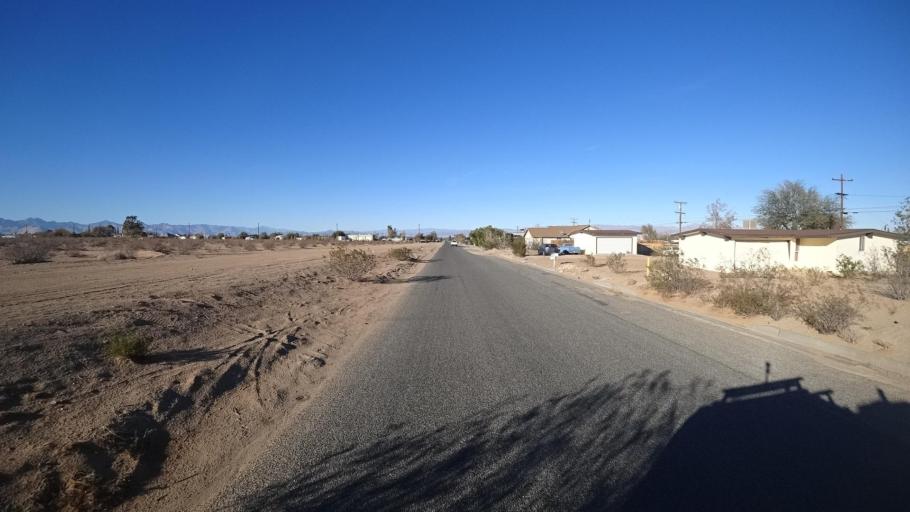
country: US
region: California
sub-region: Kern County
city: Ridgecrest
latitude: 35.5951
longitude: -117.6971
